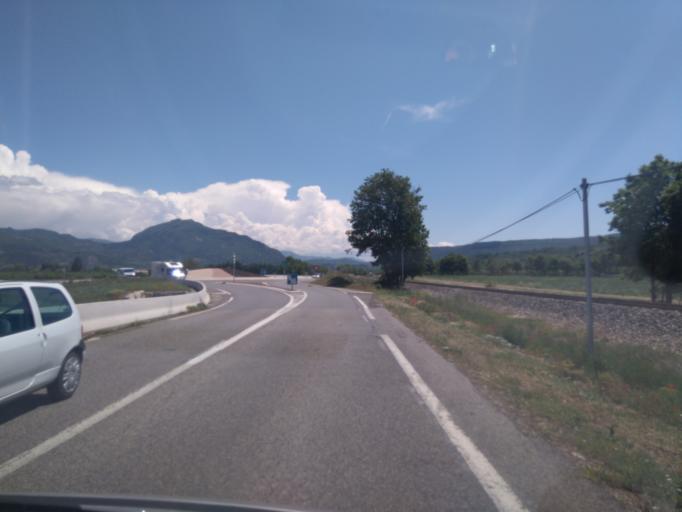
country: FR
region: Provence-Alpes-Cote d'Azur
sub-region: Departement des Alpes-de-Haute-Provence
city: Sisteron
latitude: 44.2333
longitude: 5.9039
